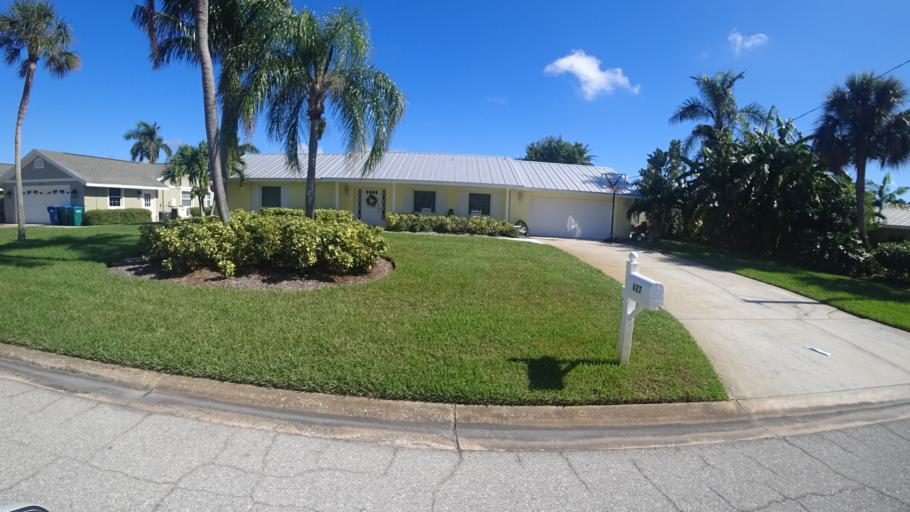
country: US
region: Florida
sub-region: Manatee County
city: Holmes Beach
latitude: 27.5198
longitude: -82.7096
